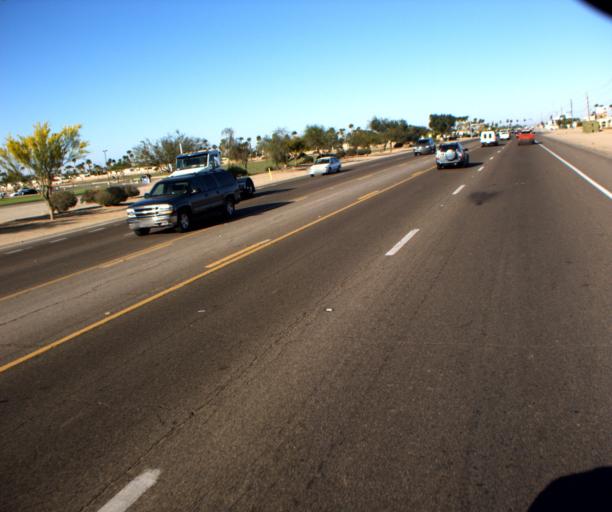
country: US
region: Arizona
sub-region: Yuma County
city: Yuma
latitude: 32.6701
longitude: -114.5267
